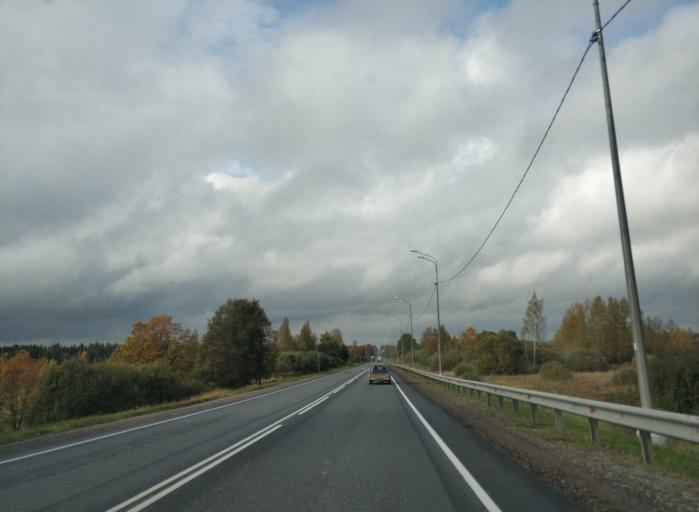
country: RU
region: Pskov
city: Ostrov
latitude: 57.1159
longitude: 28.5311
